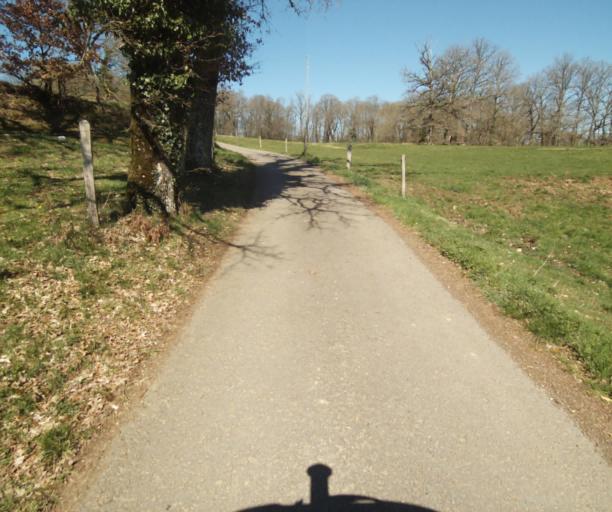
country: FR
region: Limousin
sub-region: Departement de la Correze
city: Saint-Mexant
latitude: 45.3075
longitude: 1.6448
